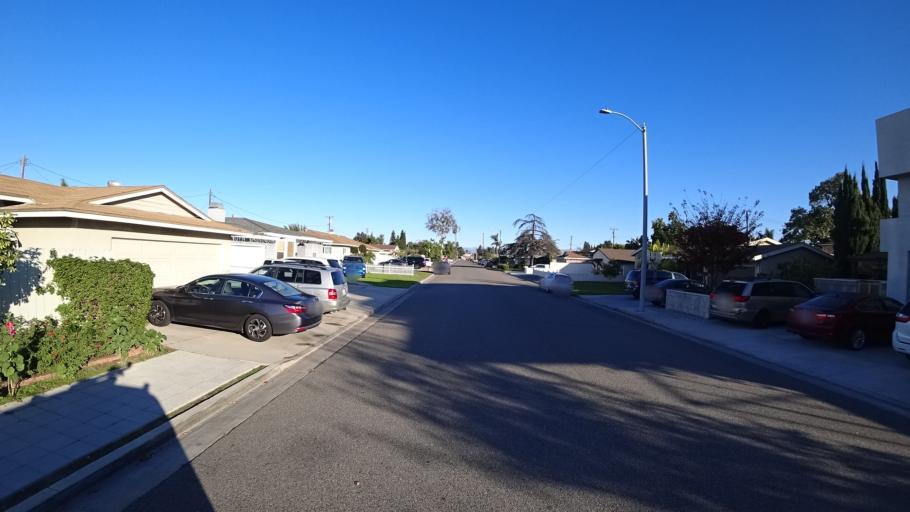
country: US
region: California
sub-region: Orange County
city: Midway City
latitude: 33.7681
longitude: -117.9742
